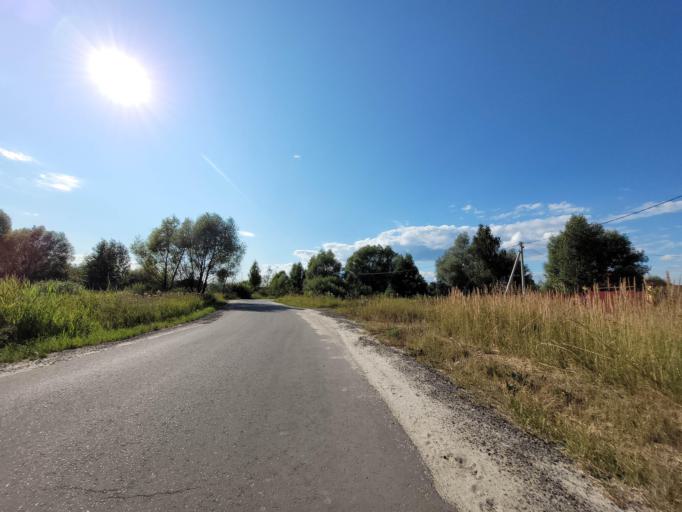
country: RU
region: Moskovskaya
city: Konobeyevo
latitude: 55.4064
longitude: 38.7046
